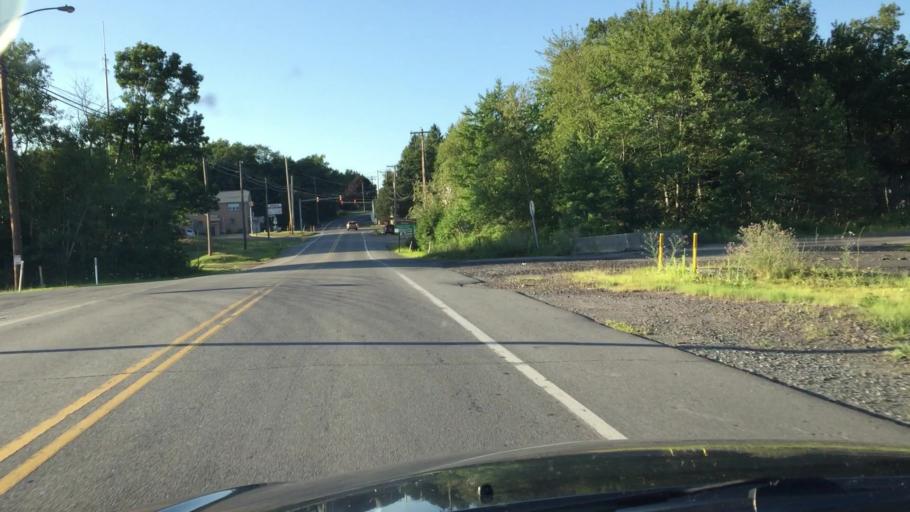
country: US
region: Pennsylvania
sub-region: Luzerne County
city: Harleigh
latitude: 40.9790
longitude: -75.9757
